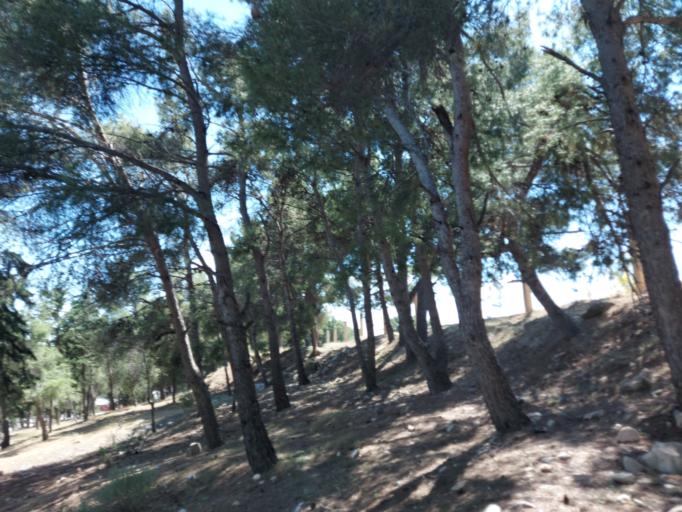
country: TN
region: Kef
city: El Kef
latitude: 36.1835
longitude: 8.7248
